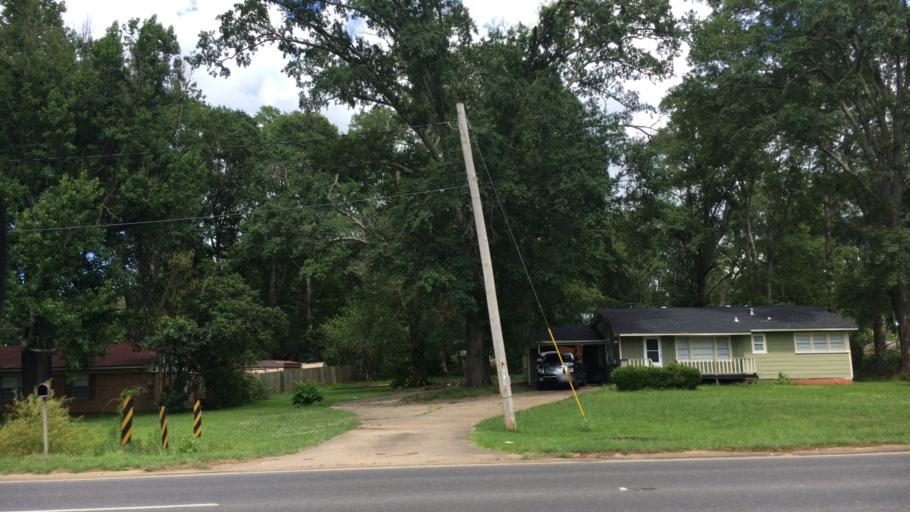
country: US
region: Louisiana
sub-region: Lincoln Parish
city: Ruston
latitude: 32.5132
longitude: -92.6383
